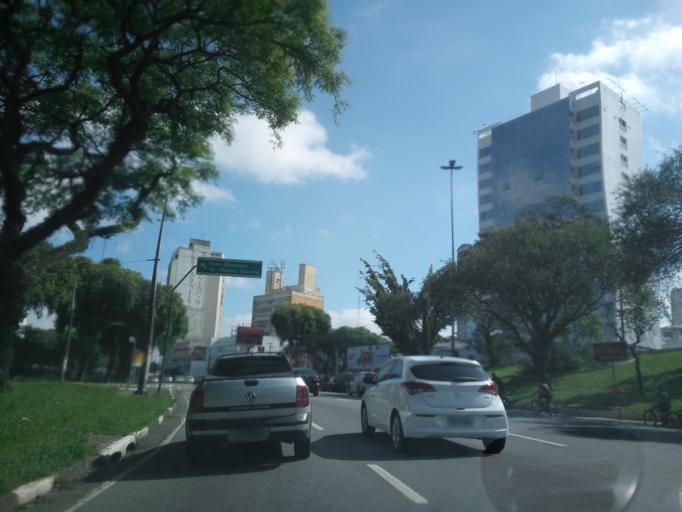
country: BR
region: Sao Paulo
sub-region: Sao Bernardo Do Campo
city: Sao Bernardo do Campo
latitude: -23.6944
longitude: -46.5526
